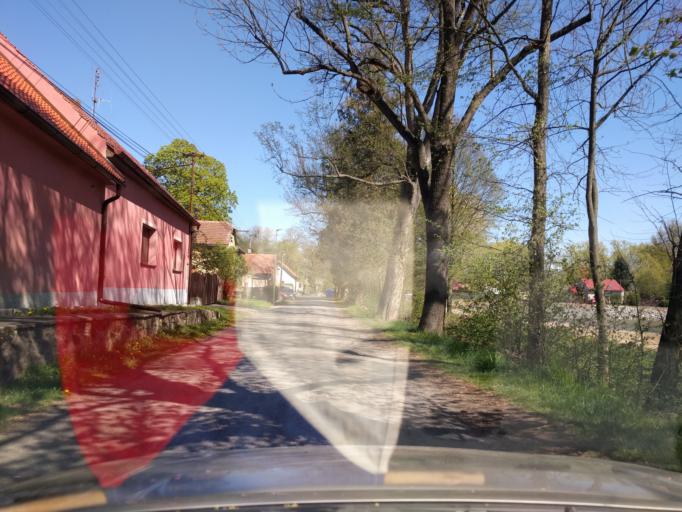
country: CZ
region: Central Bohemia
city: Cesky Brod
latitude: 50.0491
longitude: 14.8425
